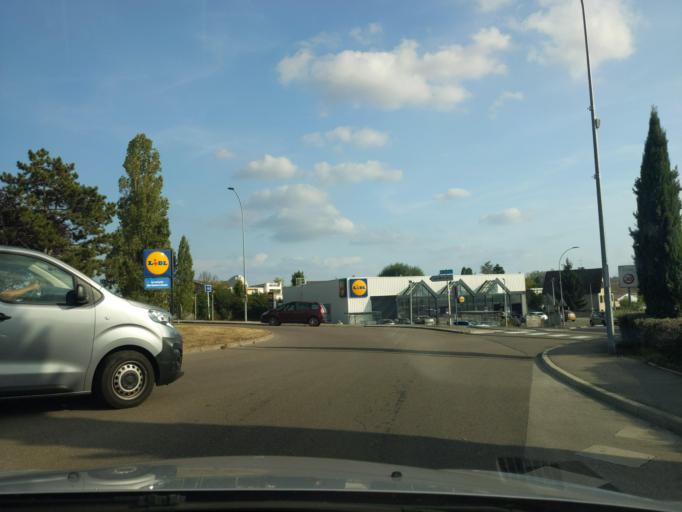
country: FR
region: Bourgogne
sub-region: Departement de la Cote-d'Or
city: Neuilly-les-Dijon
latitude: 47.2798
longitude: 5.1133
